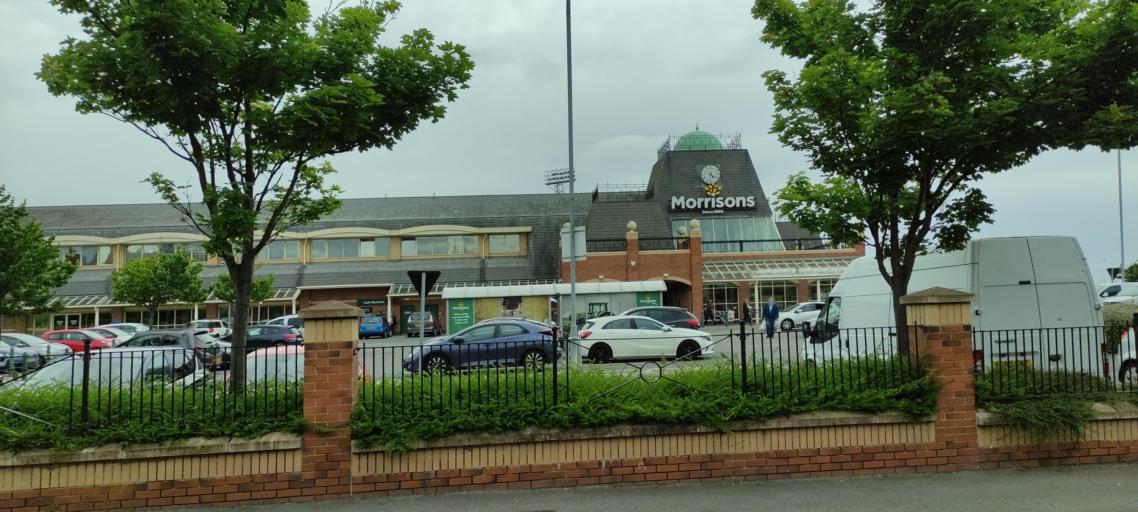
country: GB
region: England
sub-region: Hartlepool
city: Hartlepool
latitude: 54.6871
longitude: -1.2134
